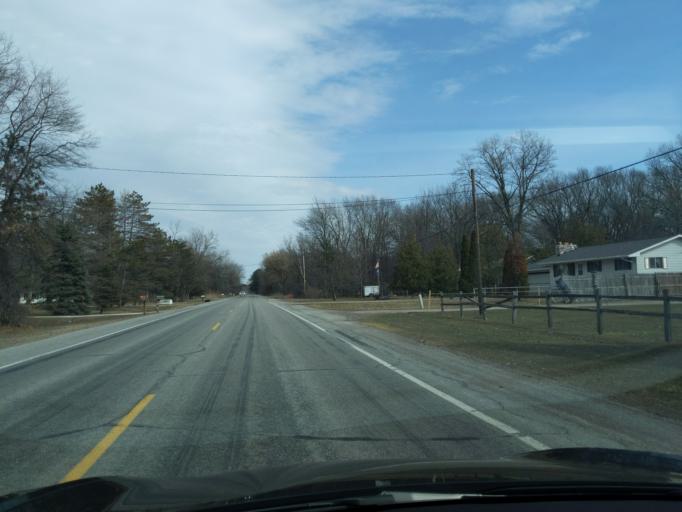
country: US
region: Michigan
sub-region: Bay County
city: Bay City
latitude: 43.6676
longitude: -83.9294
